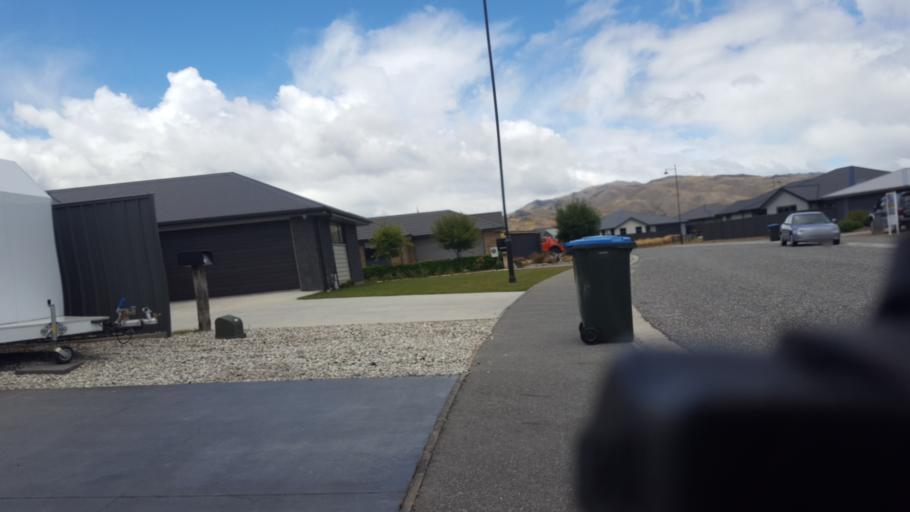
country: NZ
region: Otago
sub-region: Queenstown-Lakes District
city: Wanaka
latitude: -45.0459
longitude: 169.1791
